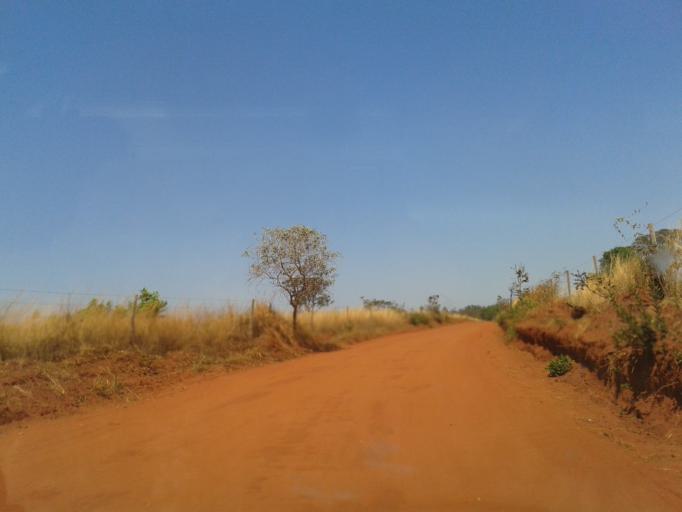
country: BR
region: Minas Gerais
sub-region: Ituiutaba
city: Ituiutaba
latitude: -19.0676
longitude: -49.3395
